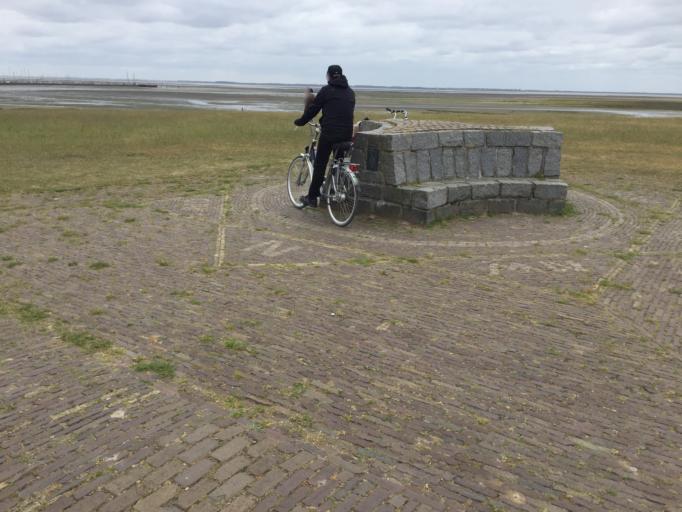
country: NL
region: Friesland
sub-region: Gemeente Schiermonnikoog
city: Schiermonnikoog
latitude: 53.4722
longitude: 6.1577
